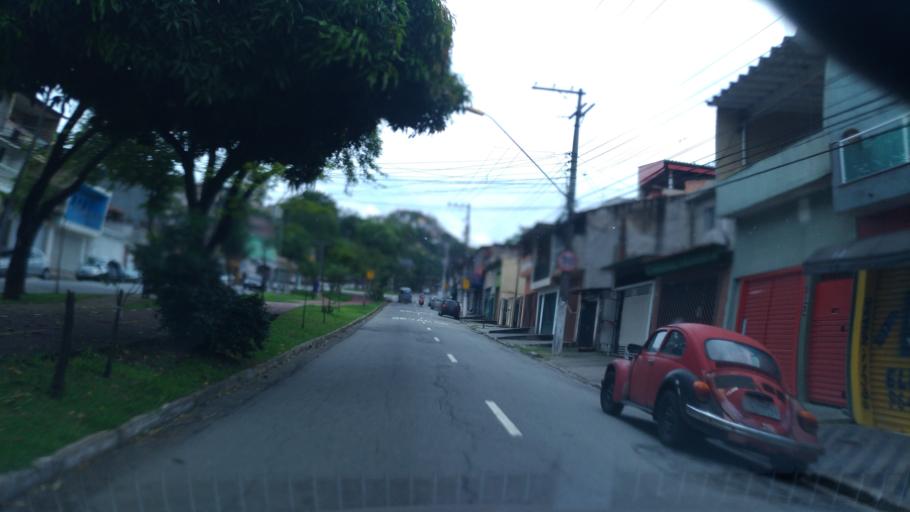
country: BR
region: Sao Paulo
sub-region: Santo Andre
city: Santo Andre
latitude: -23.6974
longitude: -46.5149
